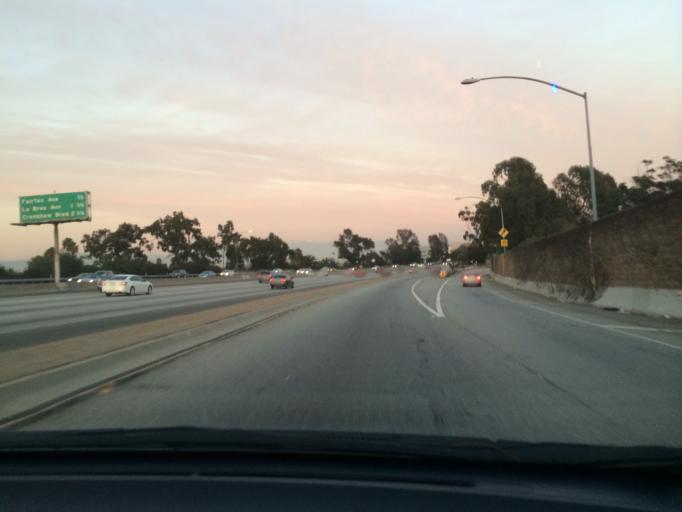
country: US
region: California
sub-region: Los Angeles County
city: Culver City
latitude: 34.0357
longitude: -118.3822
